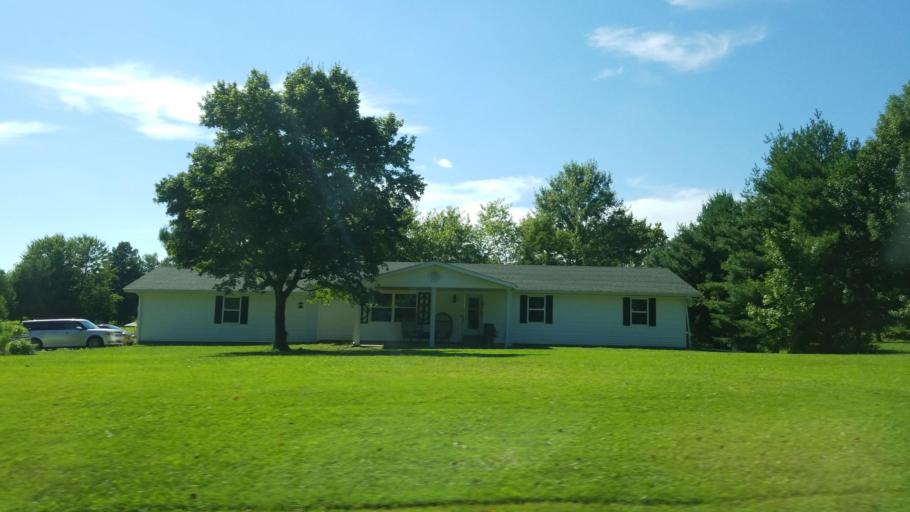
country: US
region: Illinois
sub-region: Williamson County
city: Marion
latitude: 37.7462
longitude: -88.8784
